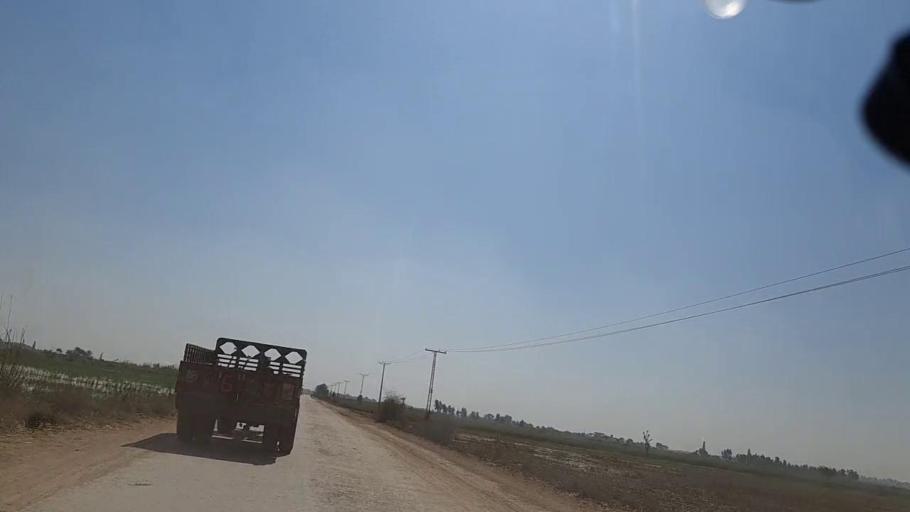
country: PK
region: Sindh
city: Mirpur Khas
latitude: 25.5014
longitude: 69.0341
